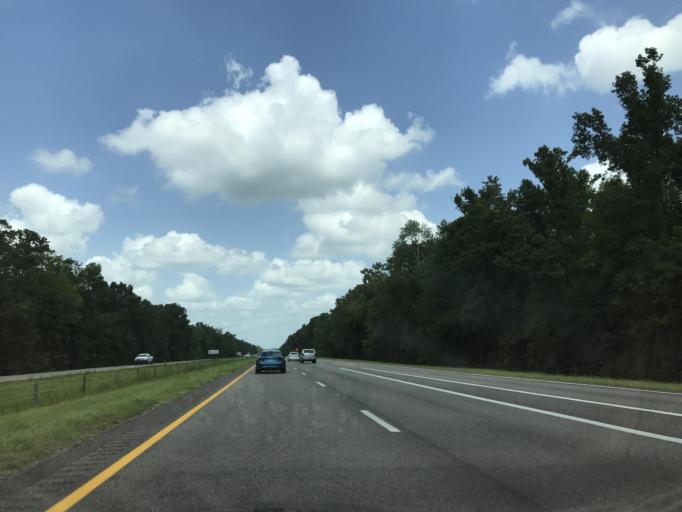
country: US
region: North Carolina
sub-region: Pender County
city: Rocky Point
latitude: 34.4450
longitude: -77.8754
